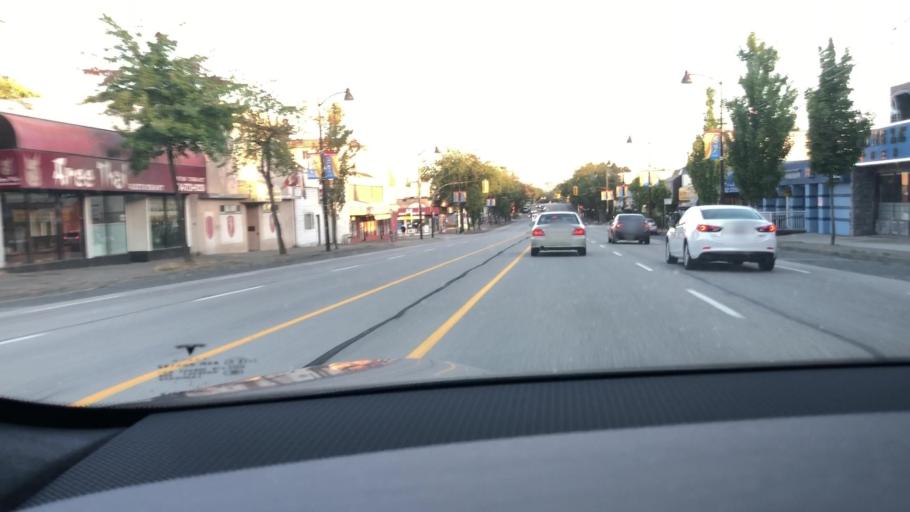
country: CA
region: British Columbia
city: Vancouver
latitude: 49.2524
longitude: -123.0806
